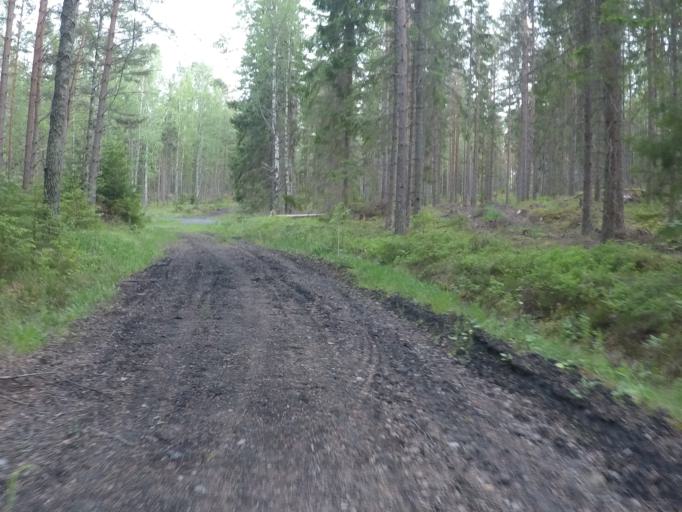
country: SE
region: Soedermanland
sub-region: Eskilstuna Kommun
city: Kvicksund
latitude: 59.4063
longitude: 16.3210
